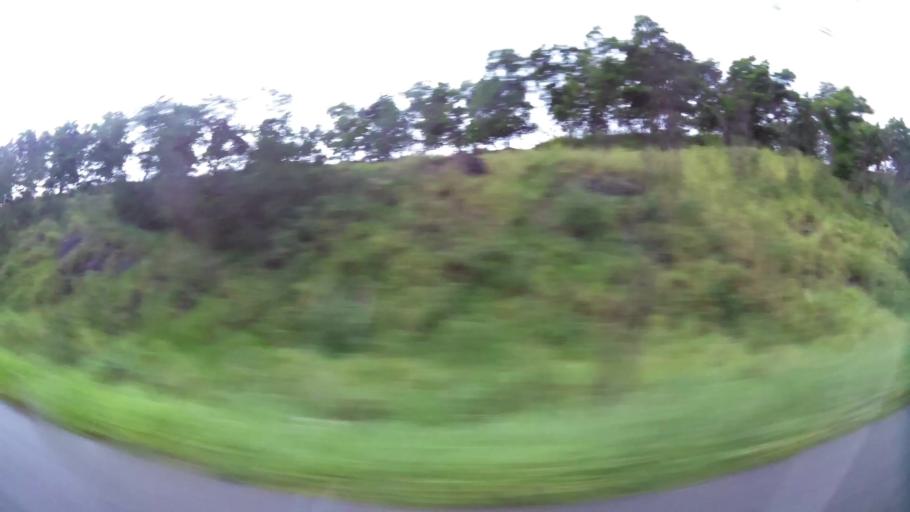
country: DO
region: San Cristobal
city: Villa Altagracia
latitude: 18.6081
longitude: -70.1466
